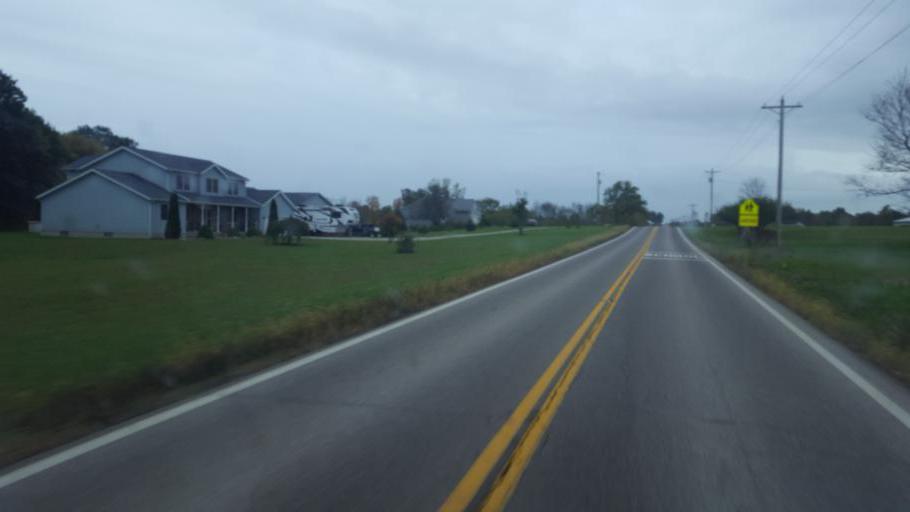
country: US
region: Ohio
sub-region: Ashland County
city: Ashland
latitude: 40.9274
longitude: -82.3969
